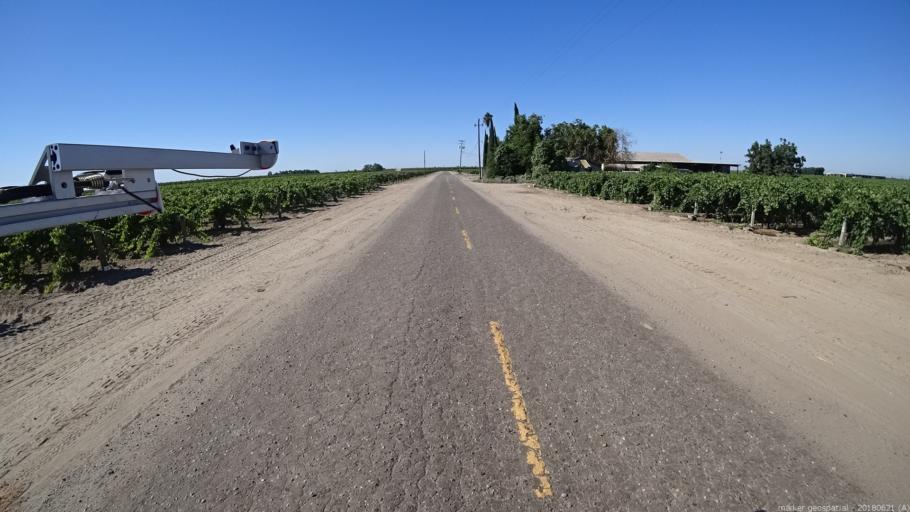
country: US
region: California
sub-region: Fresno County
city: Biola
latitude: 36.8410
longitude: -120.0463
